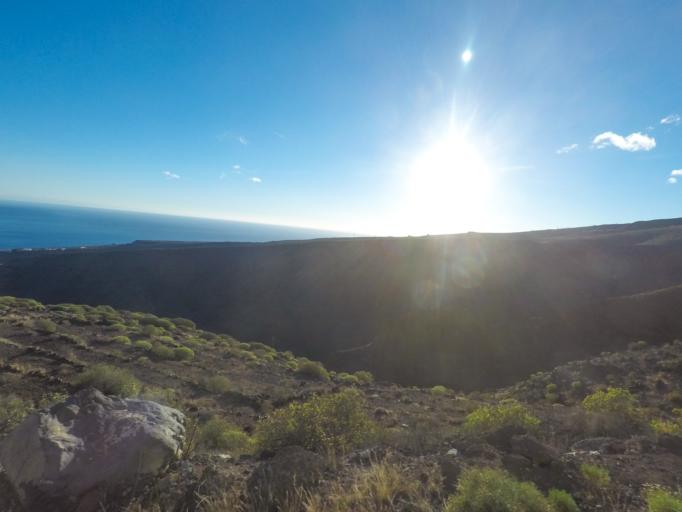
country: ES
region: Canary Islands
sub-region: Provincia de Santa Cruz de Tenerife
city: Alajero
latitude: 28.0511
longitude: -17.2006
